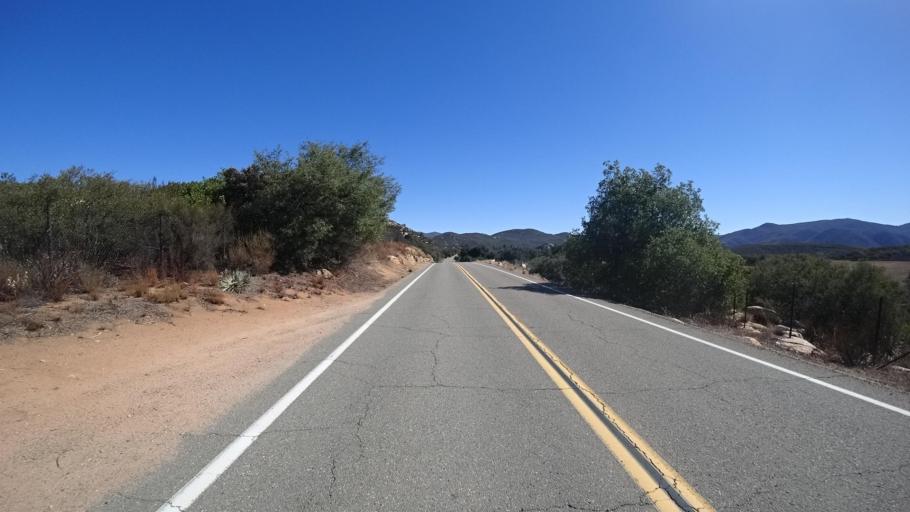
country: US
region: California
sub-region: San Diego County
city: Descanso
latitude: 32.7976
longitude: -116.6542
